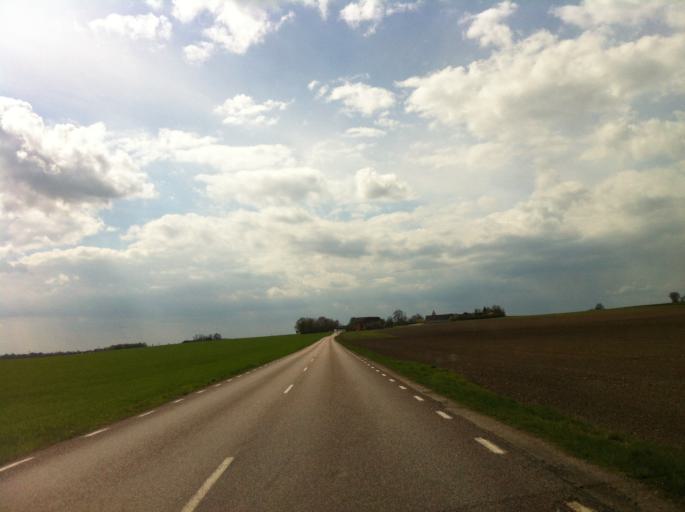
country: SE
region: Skane
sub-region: Eslovs Kommun
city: Eslov
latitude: 55.8300
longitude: 13.2051
